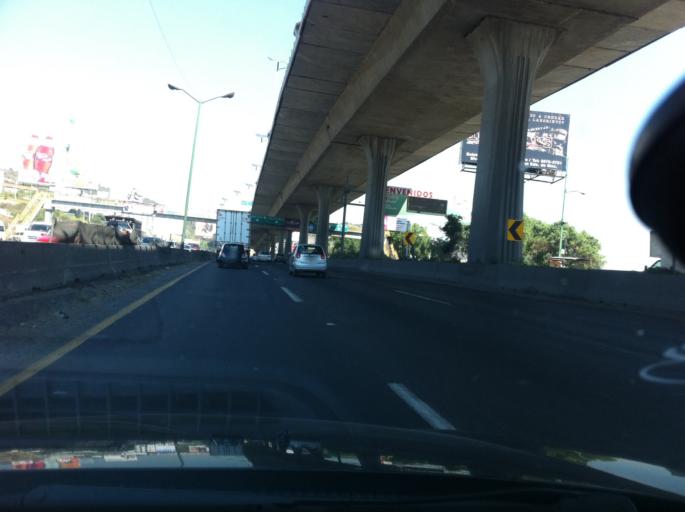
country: MX
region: Mexico
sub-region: Tultitlan
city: Buenavista
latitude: 19.5900
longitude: -99.2016
